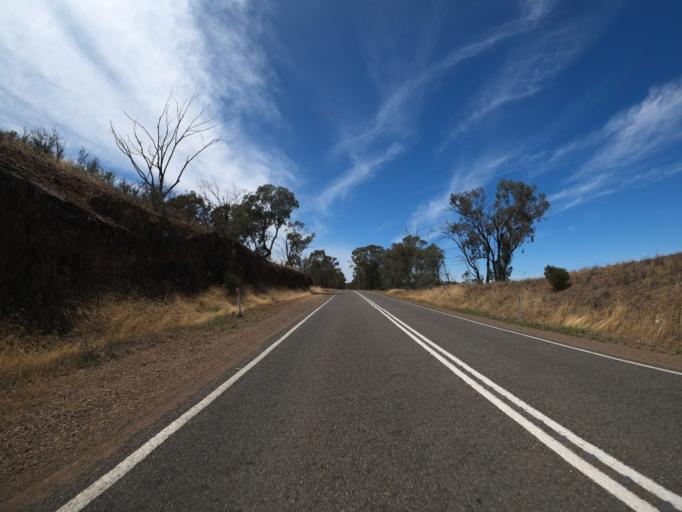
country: AU
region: Victoria
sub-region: Benalla
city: Benalla
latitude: -36.3490
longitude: 145.9620
